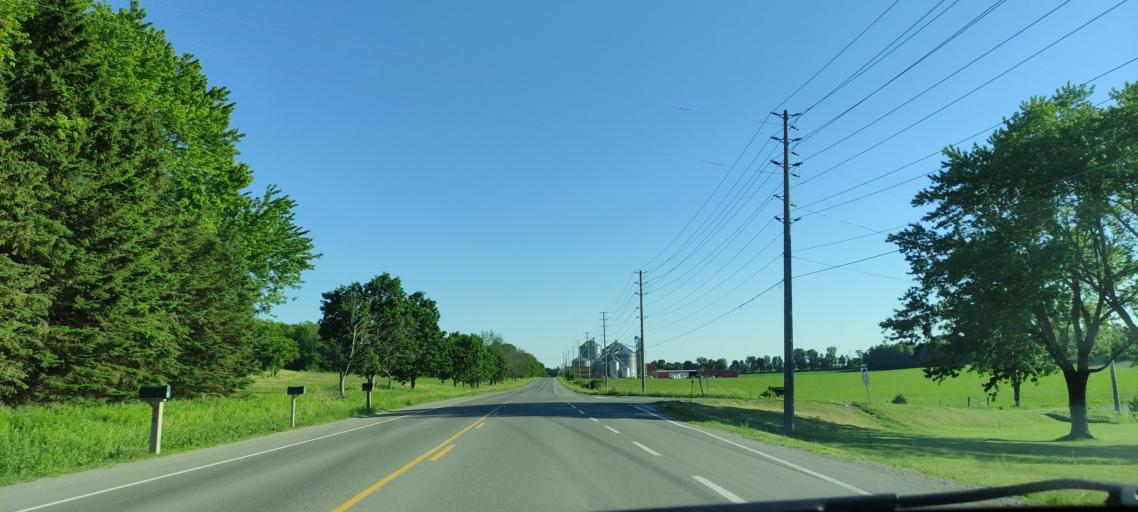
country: CA
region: Ontario
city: Quinte West
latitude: 44.2279
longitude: -77.8230
